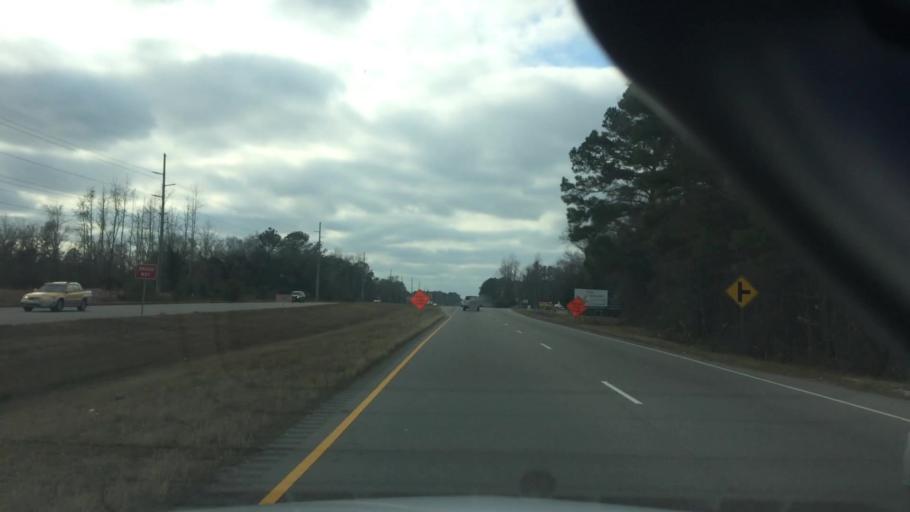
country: US
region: North Carolina
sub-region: Brunswick County
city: Shallotte
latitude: 33.9902
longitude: -78.3509
